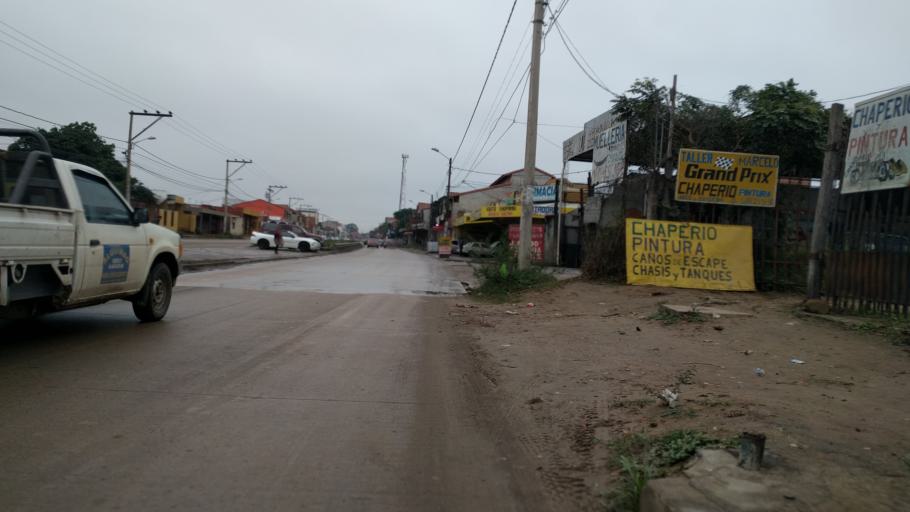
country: BO
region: Santa Cruz
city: Santa Cruz de la Sierra
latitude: -17.8260
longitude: -63.1683
